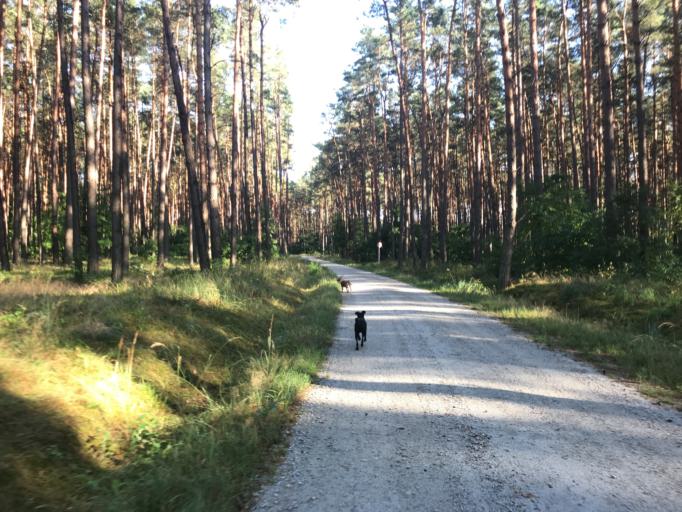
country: PL
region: Greater Poland Voivodeship
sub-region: Powiat szamotulski
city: Obrzycko
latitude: 52.7334
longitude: 16.5893
